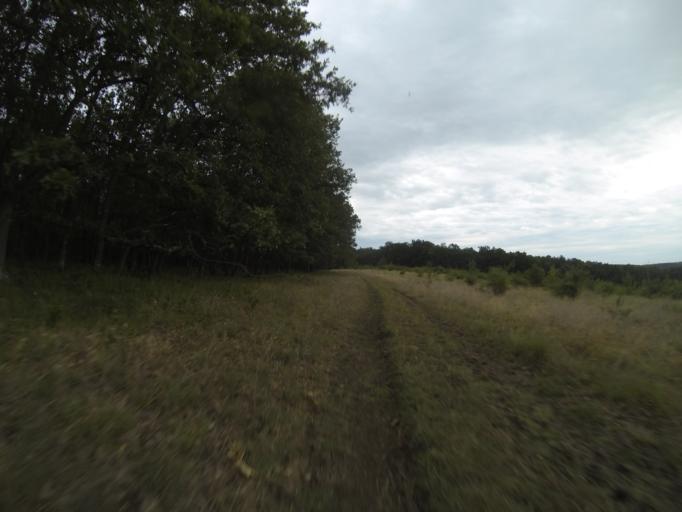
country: RO
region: Dolj
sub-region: Comuna Bradesti
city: Bradesti
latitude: 44.5271
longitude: 23.6591
